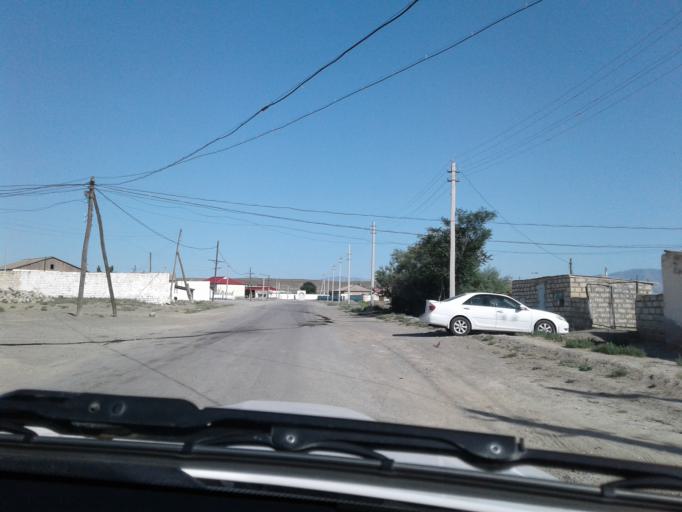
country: TM
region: Balkan
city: Serdar
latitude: 38.7129
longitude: 56.3376
